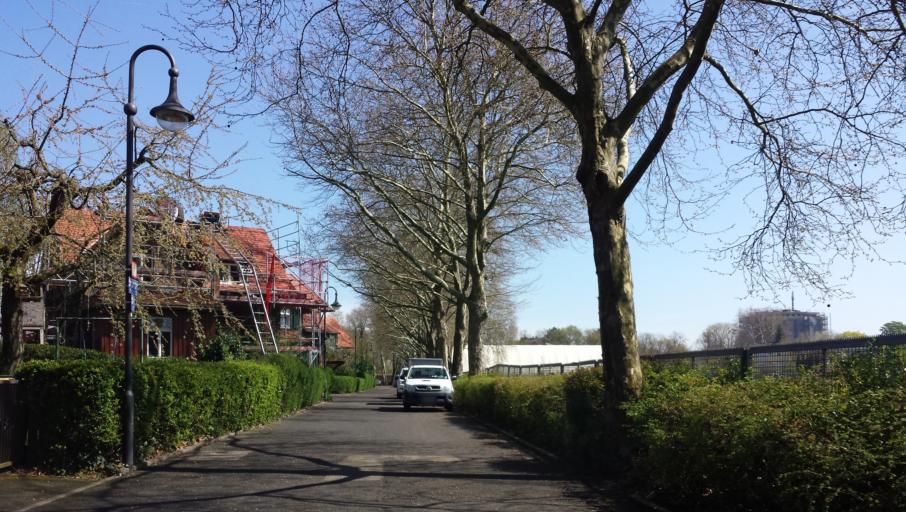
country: DE
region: Hesse
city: Sulzbach
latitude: 50.1023
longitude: 8.5304
